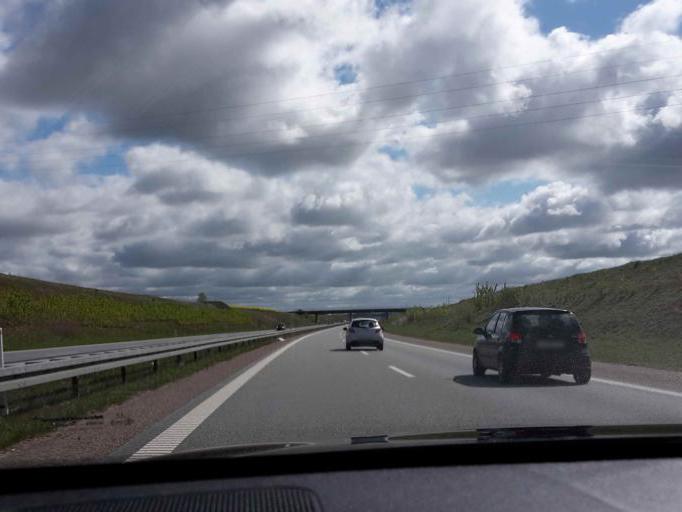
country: DK
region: Central Jutland
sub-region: Arhus Kommune
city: Lystrup
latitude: 56.2217
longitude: 10.2005
